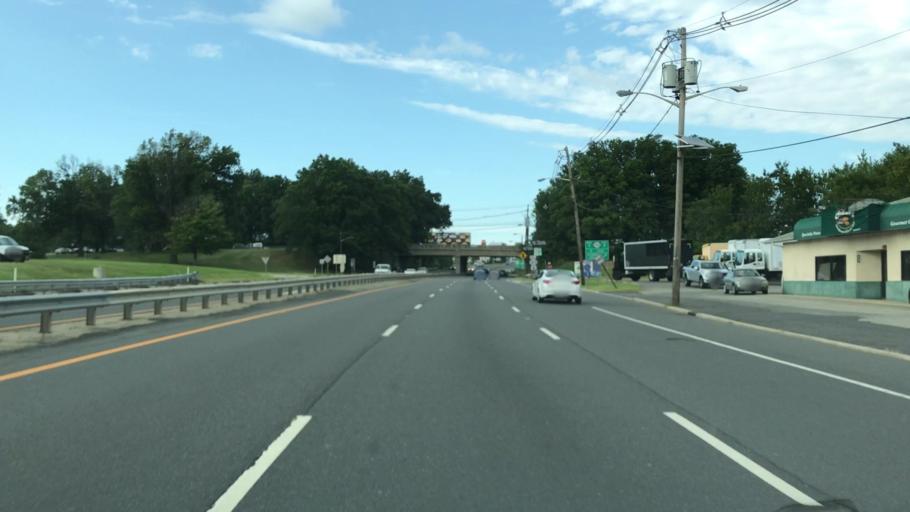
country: US
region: New Jersey
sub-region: Middlesex County
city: Fords
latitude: 40.5326
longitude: -74.2974
